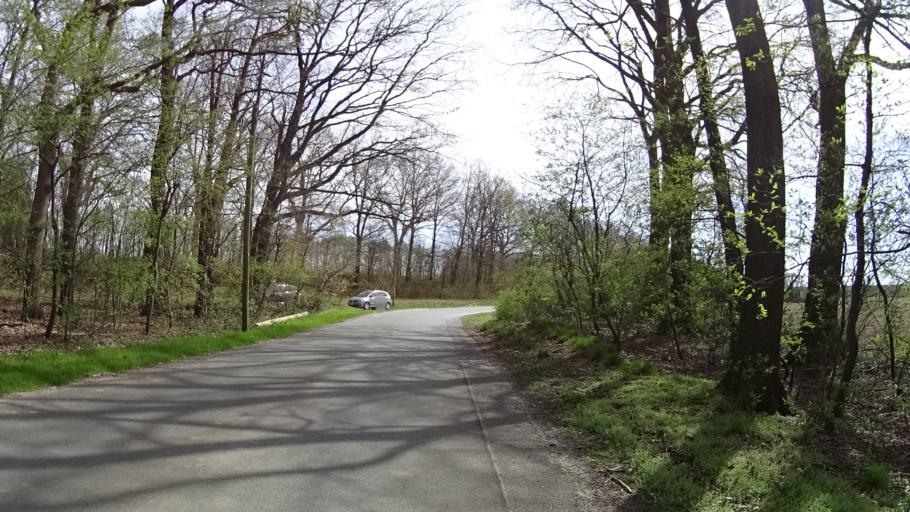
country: DE
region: Lower Saxony
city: Emsburen
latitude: 52.4304
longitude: 7.3532
